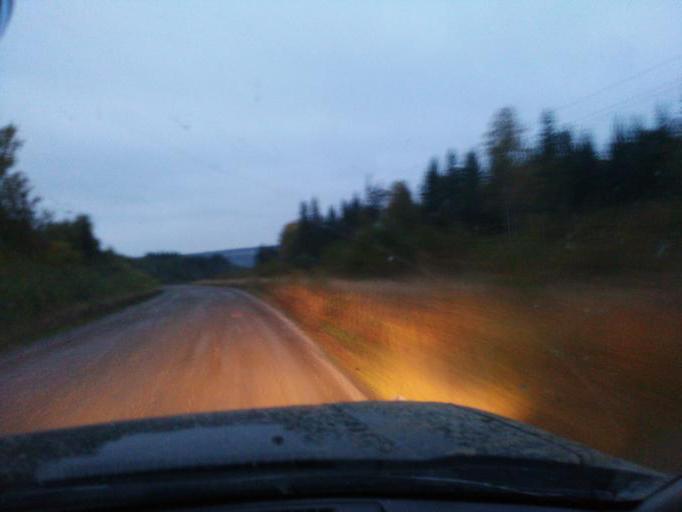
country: RU
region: Perm
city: Gornozavodsk
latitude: 57.9056
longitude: 58.3801
